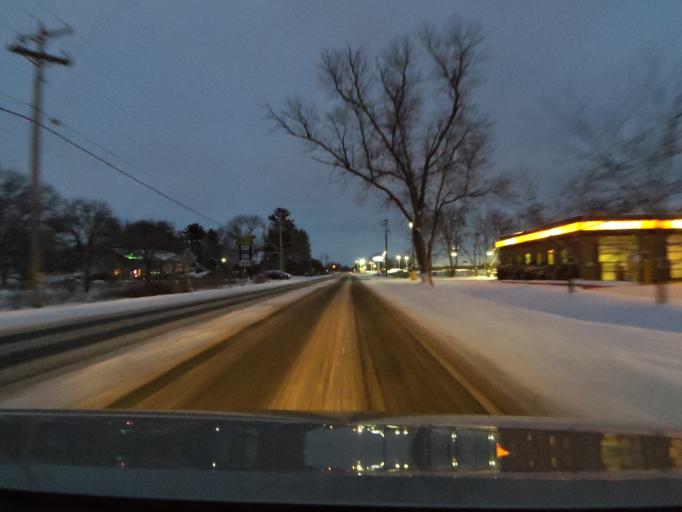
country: US
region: Wisconsin
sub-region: Dunn County
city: Menomonie
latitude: 44.9046
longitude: -91.9372
